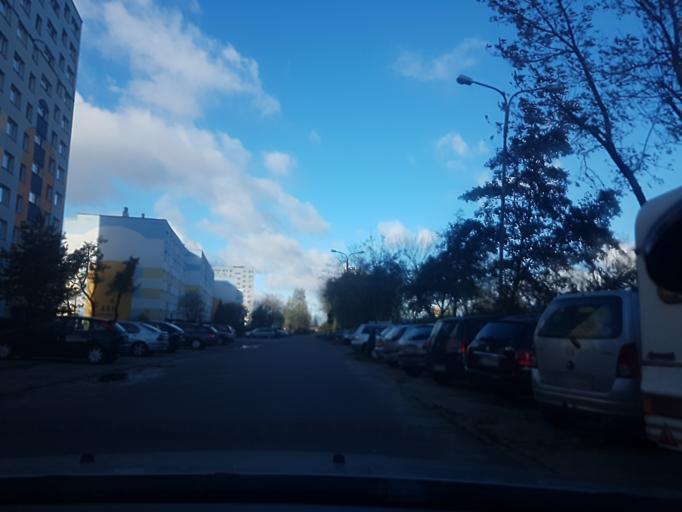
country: PL
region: Lodz Voivodeship
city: Lodz
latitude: 51.7605
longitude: 19.5344
